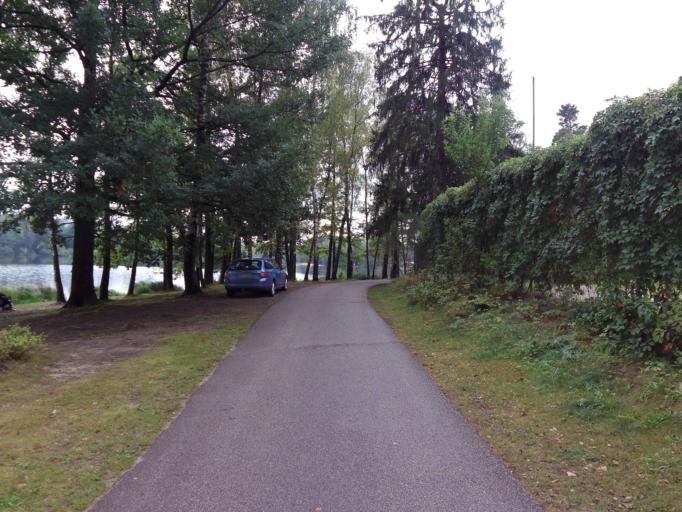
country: CZ
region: Jihocesky
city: Chlum u Trebone
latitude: 48.9789
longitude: 14.9593
